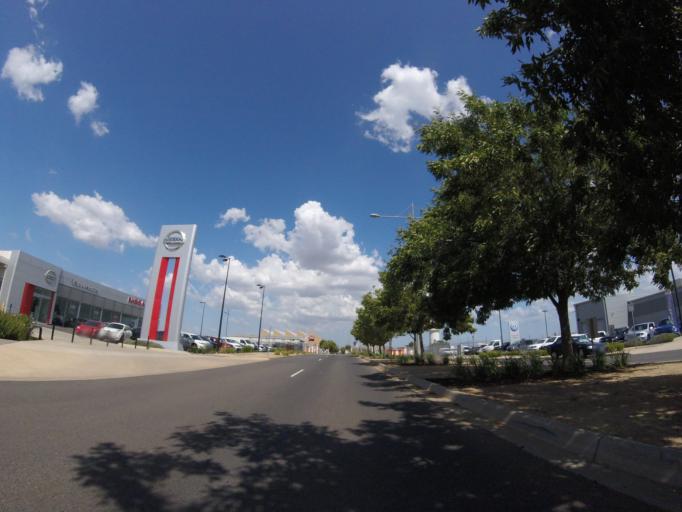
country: AU
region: Victoria
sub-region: Moreland
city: Gowanbrae
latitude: -37.7201
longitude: 144.8953
